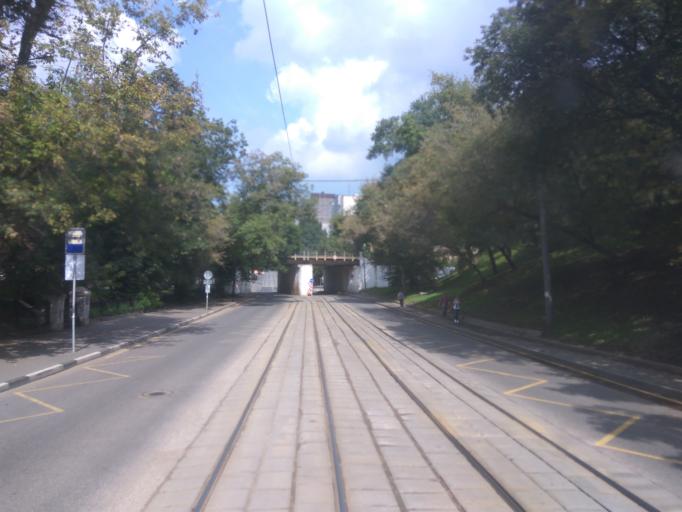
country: RU
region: Moscow
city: Taganskiy
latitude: 55.7487
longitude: 37.6757
